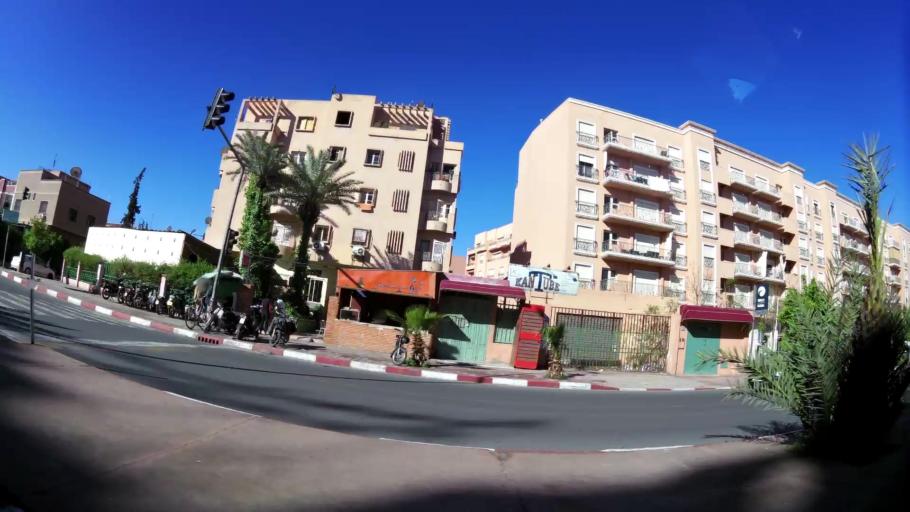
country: MA
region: Marrakech-Tensift-Al Haouz
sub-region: Marrakech
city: Marrakesh
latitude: 31.6456
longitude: -8.0103
